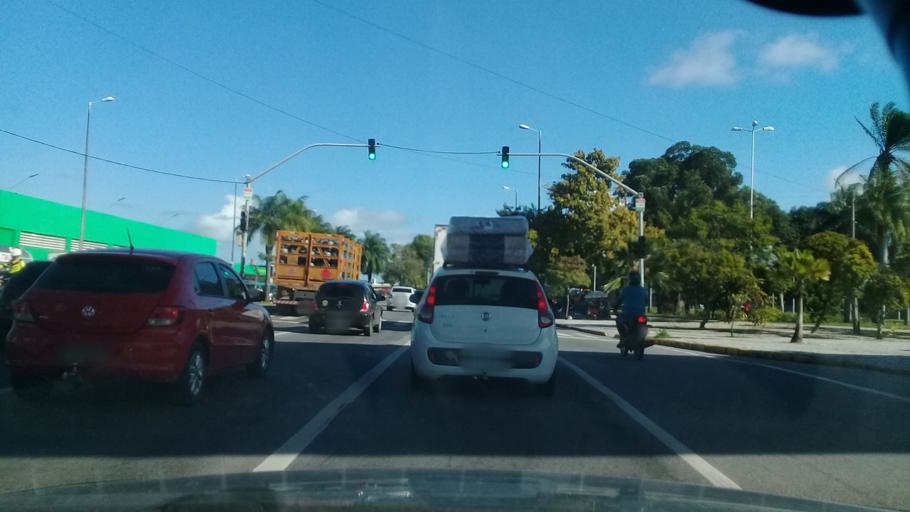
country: BR
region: Pernambuco
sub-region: Recife
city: Recife
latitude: -8.1323
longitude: -34.9164
